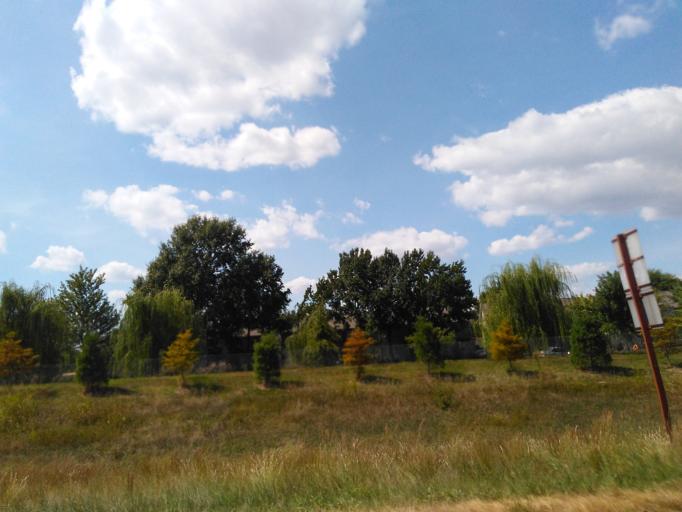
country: US
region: Illinois
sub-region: Saint Clair County
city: Dupo
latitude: 38.5172
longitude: -90.2005
